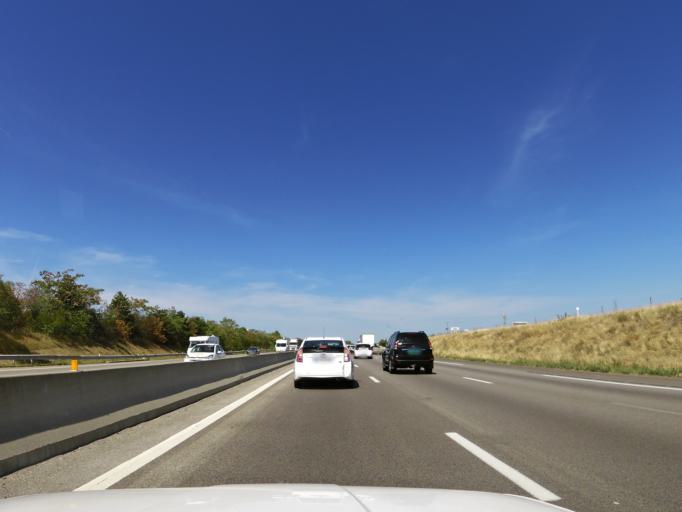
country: FR
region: Rhone-Alpes
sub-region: Departement de la Drome
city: Portes-les-Valence
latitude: 44.8731
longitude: 4.8648
